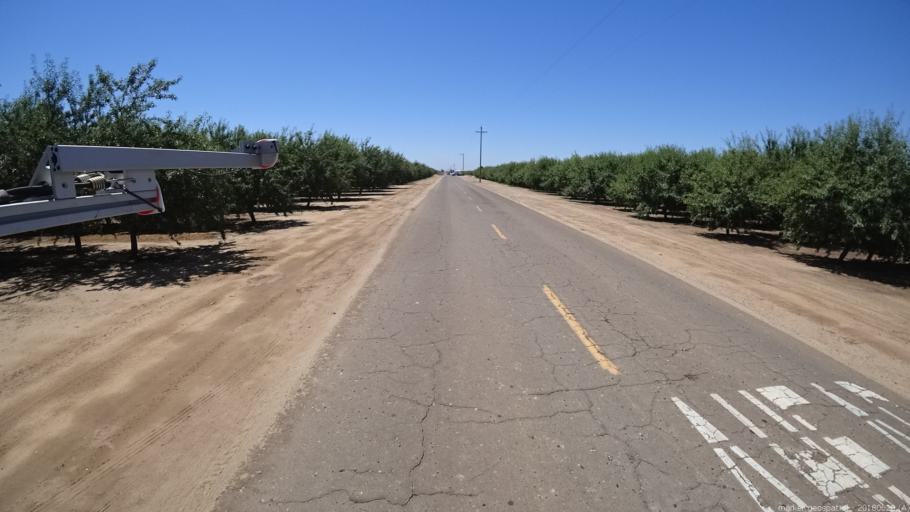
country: US
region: California
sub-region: Fresno County
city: Biola
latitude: 36.8675
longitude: -119.9744
